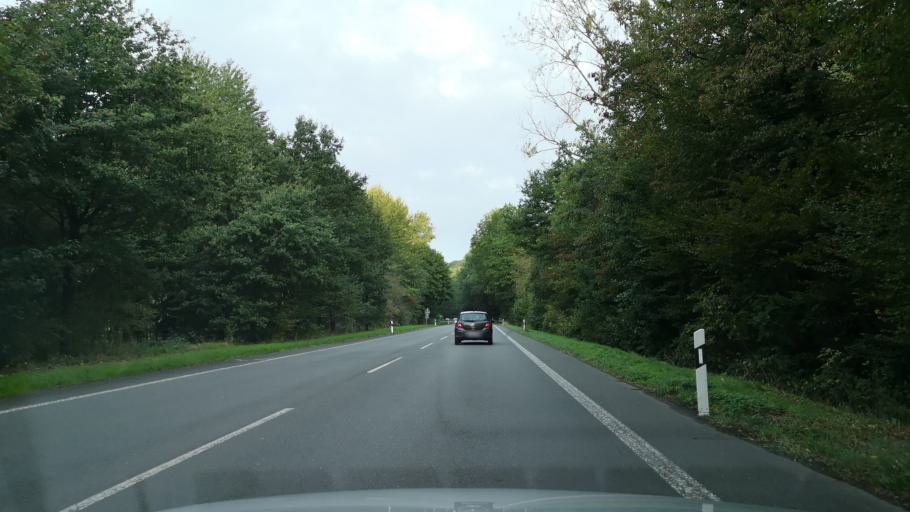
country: DE
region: North Rhine-Westphalia
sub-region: Regierungsbezirk Arnsberg
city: Hagen
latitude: 51.3908
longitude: 7.5187
